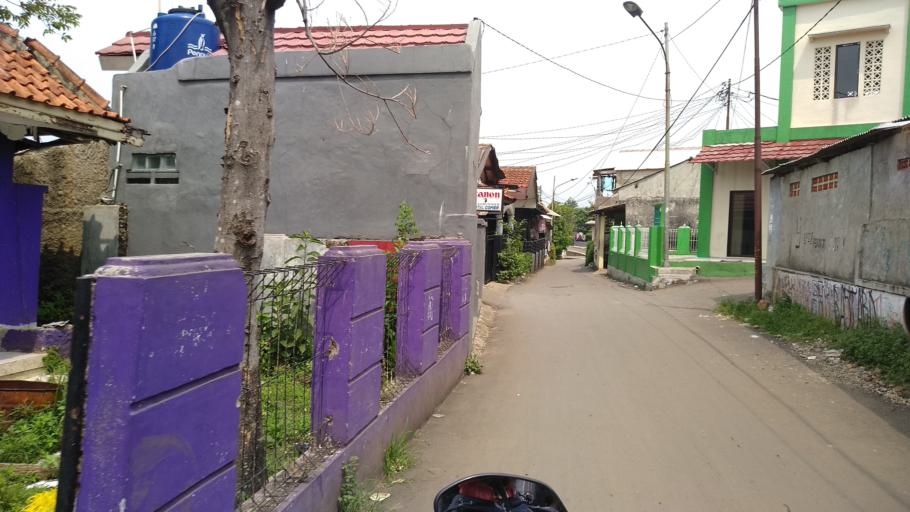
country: ID
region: West Java
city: Ciampea
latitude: -6.5583
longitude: 106.7470
